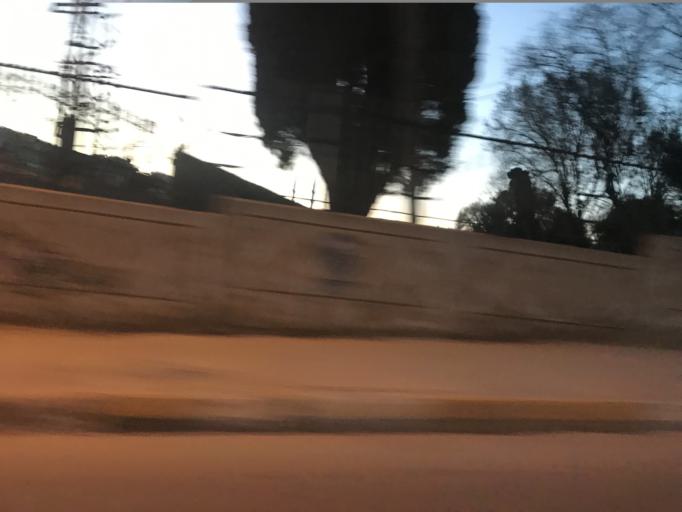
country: TR
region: Istanbul
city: Pendik
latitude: 40.9002
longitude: 29.2721
